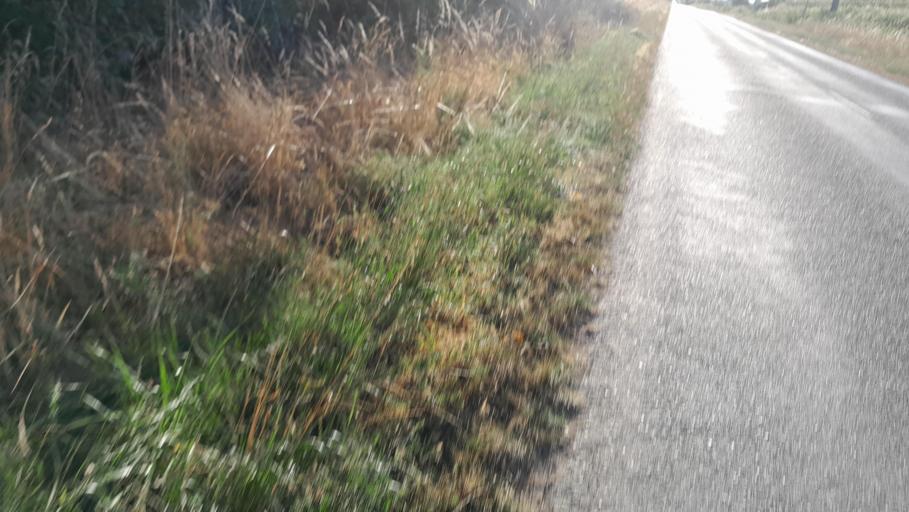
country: FR
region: Brittany
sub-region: Departement d'Ille-et-Vilaine
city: Le Pertre
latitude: 47.9669
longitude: -1.0645
